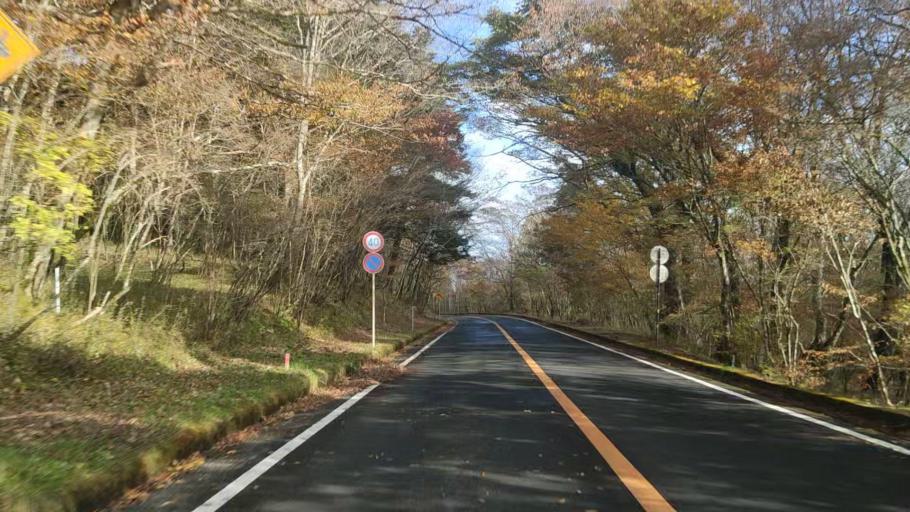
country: JP
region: Shizuoka
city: Fujinomiya
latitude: 35.2948
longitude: 138.7125
